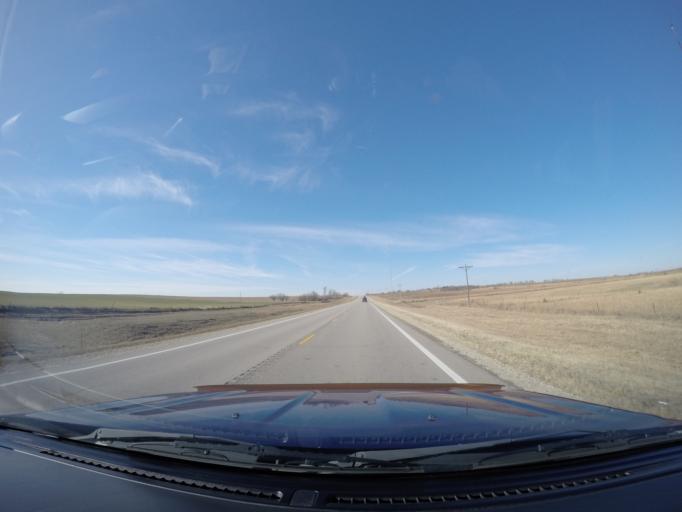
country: US
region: Kansas
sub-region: Clay County
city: Clay Center
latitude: 39.3795
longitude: -97.2574
